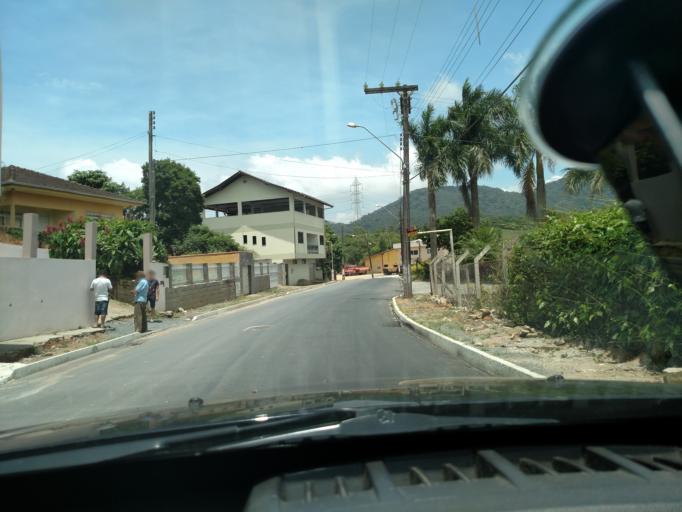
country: BR
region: Santa Catarina
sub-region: Gaspar
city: Gaspar
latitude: -26.9053
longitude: -48.8227
